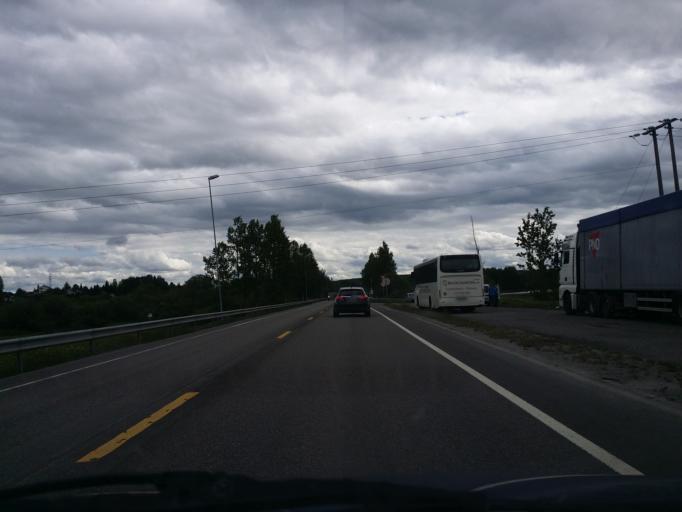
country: NO
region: Hedmark
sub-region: Hamar
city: Hamar
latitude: 60.8061
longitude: 11.1099
